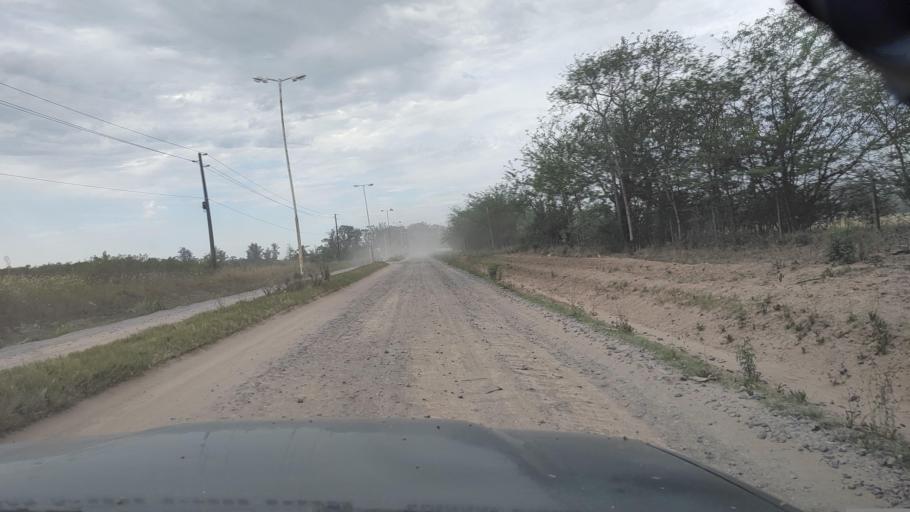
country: AR
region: Buenos Aires
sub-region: Partido de Lujan
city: Lujan
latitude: -34.5485
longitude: -59.0837
